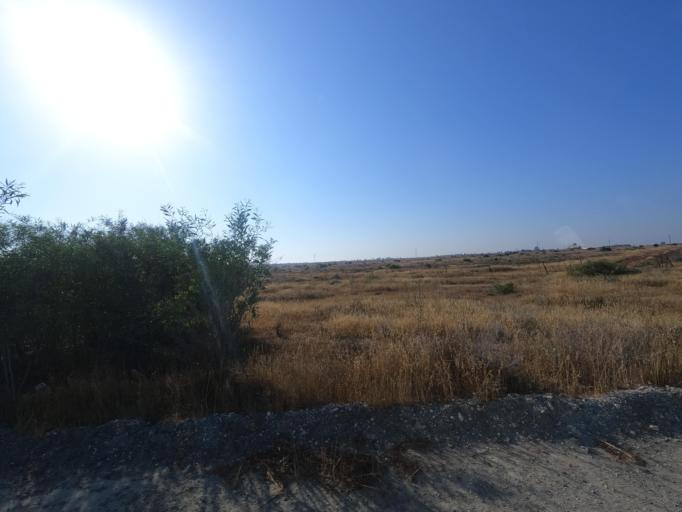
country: CY
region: Ammochostos
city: Frenaros
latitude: 35.0774
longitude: 33.9022
